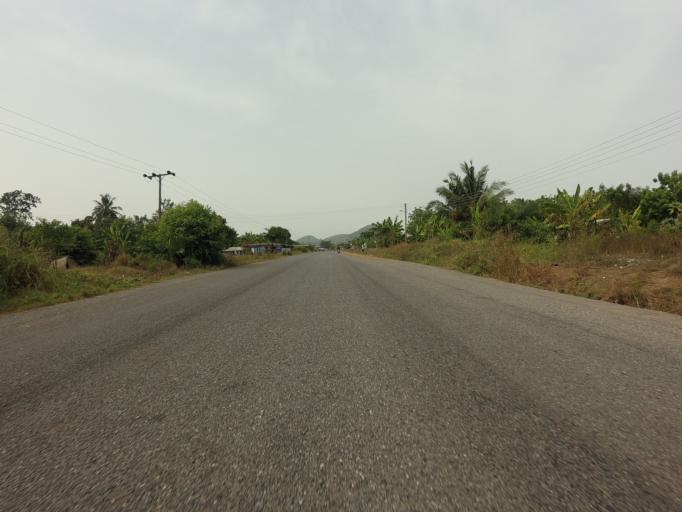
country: GH
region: Volta
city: Ho
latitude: 6.4181
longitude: 0.1769
